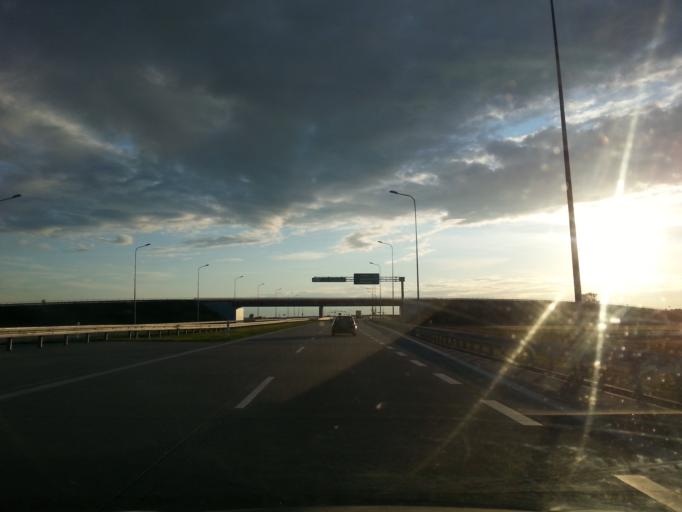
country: PL
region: Lodz Voivodeship
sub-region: Powiat wieruszowski
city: Walichnowy
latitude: 51.3148
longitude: 18.4038
